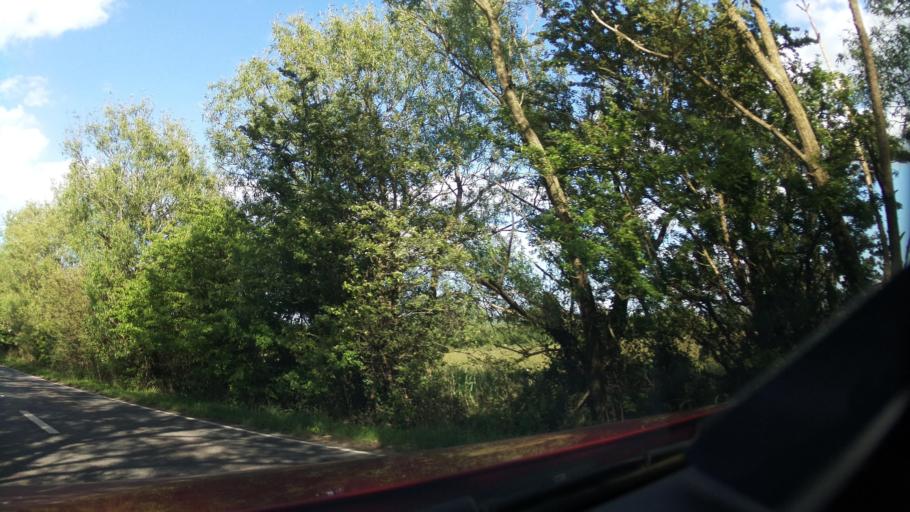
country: GB
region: England
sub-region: Somerset
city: Westonzoyland
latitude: 51.0625
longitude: -2.9307
